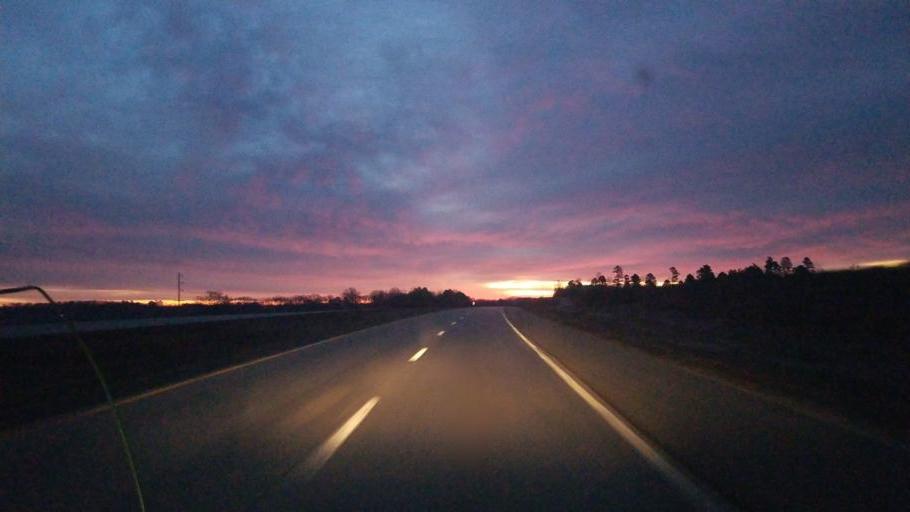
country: US
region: Missouri
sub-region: Shannon County
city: Winona
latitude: 36.9989
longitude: -91.4683
